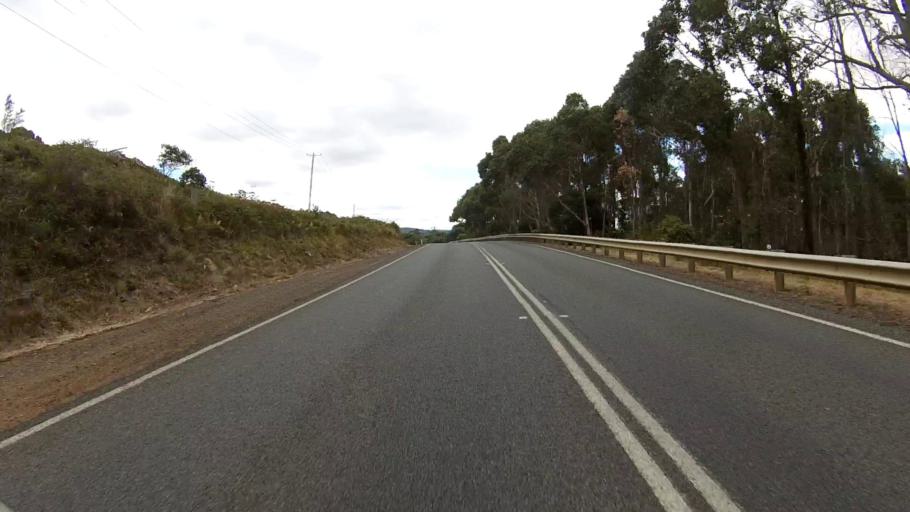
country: AU
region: Tasmania
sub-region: Sorell
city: Sorell
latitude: -42.6627
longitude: 147.5326
